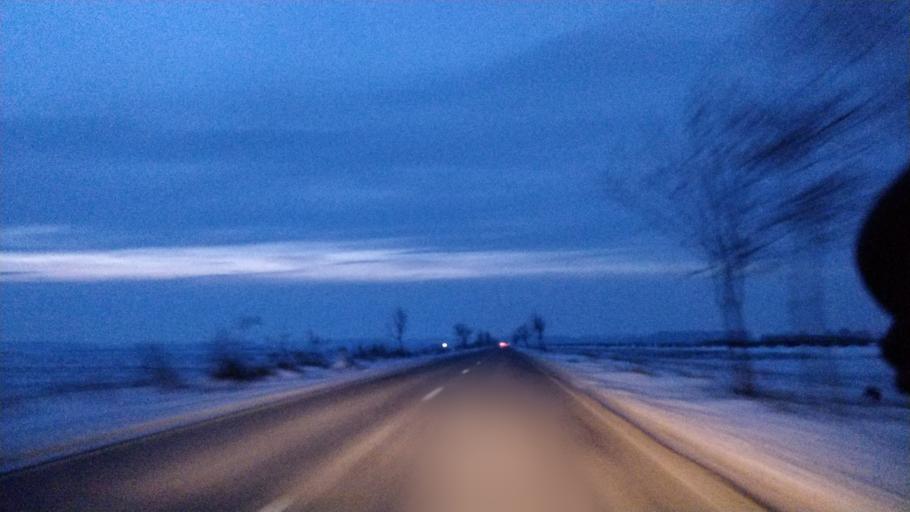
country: RO
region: Vrancea
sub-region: Comuna Suraia
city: Suraia
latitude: 45.6415
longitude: 27.3648
